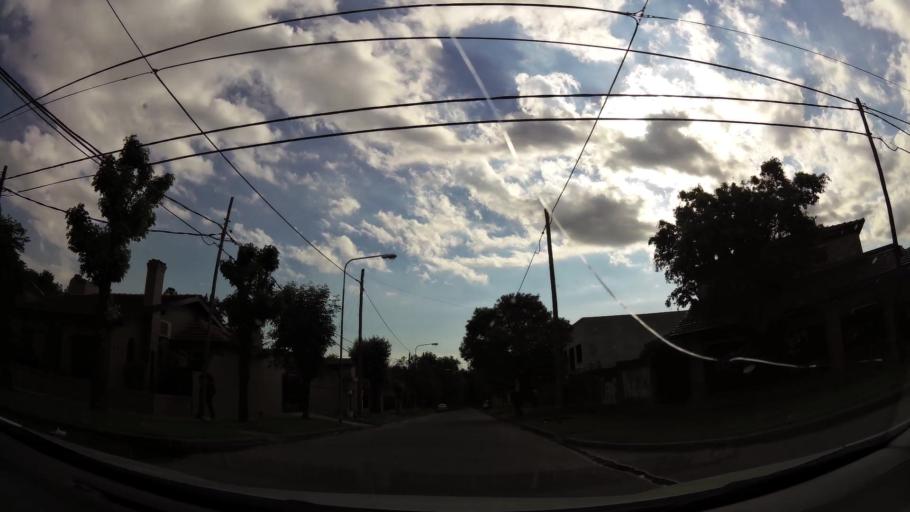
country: AR
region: Buenos Aires
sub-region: Partido de Tigre
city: Tigre
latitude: -34.4704
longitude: -58.6560
